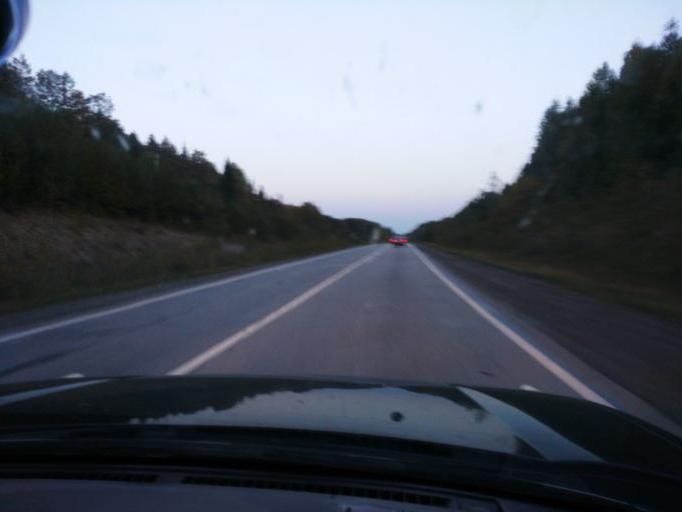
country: RU
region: Perm
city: Verkhnechusovskiye Gorodki
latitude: 58.2755
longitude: 56.9374
